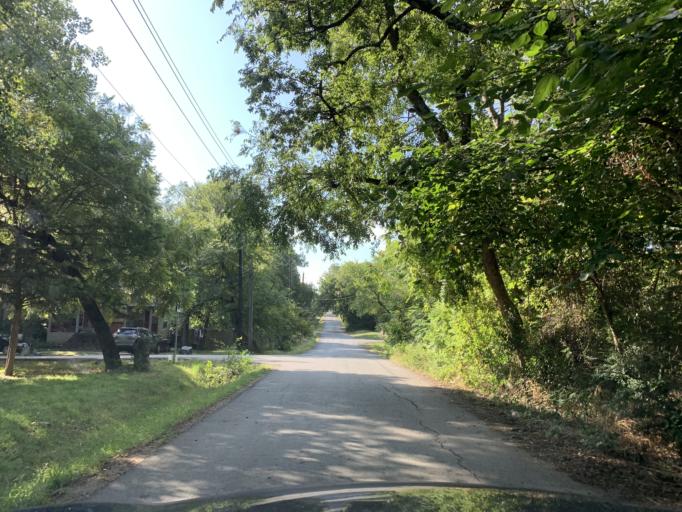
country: US
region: Texas
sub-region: Dallas County
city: Hutchins
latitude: 32.6783
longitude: -96.7787
